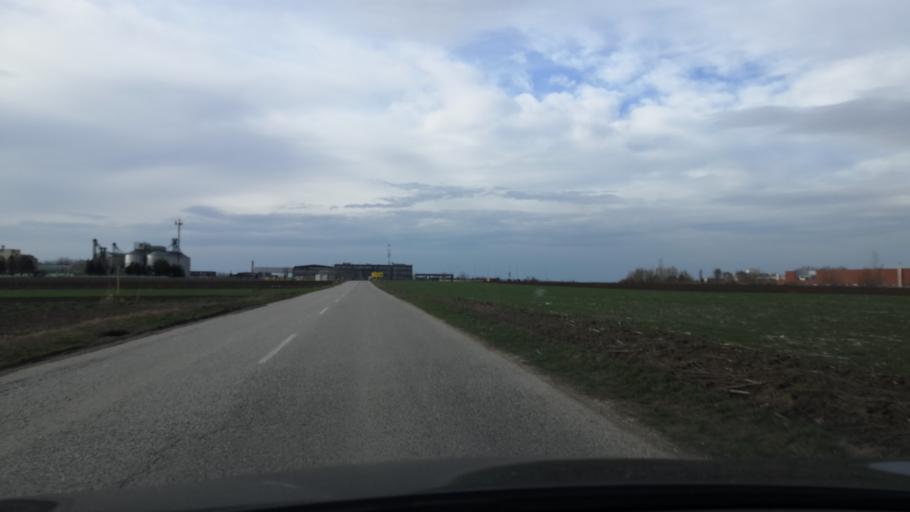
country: RS
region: Autonomna Pokrajina Vojvodina
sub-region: Sremski Okrug
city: Ingija
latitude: 45.0519
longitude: 20.1058
